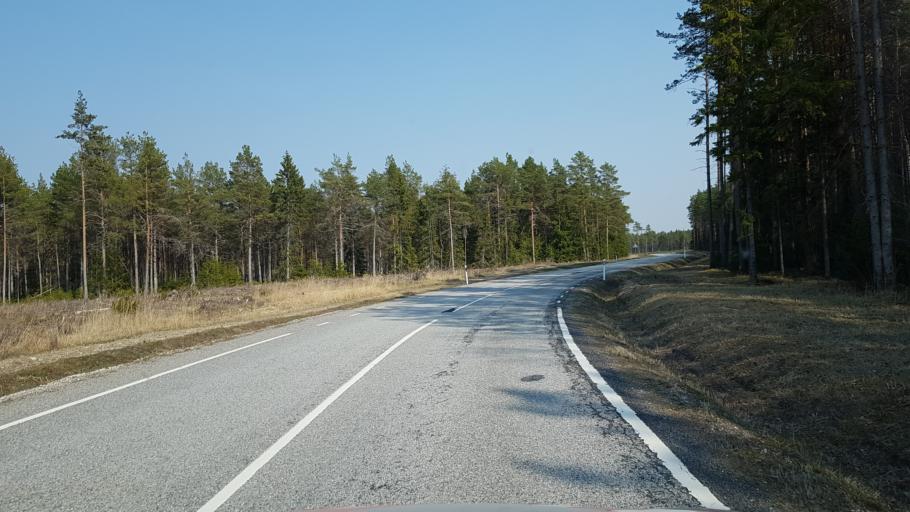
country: EE
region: Harju
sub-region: Paldiski linn
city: Paldiski
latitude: 59.2502
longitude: 23.7774
